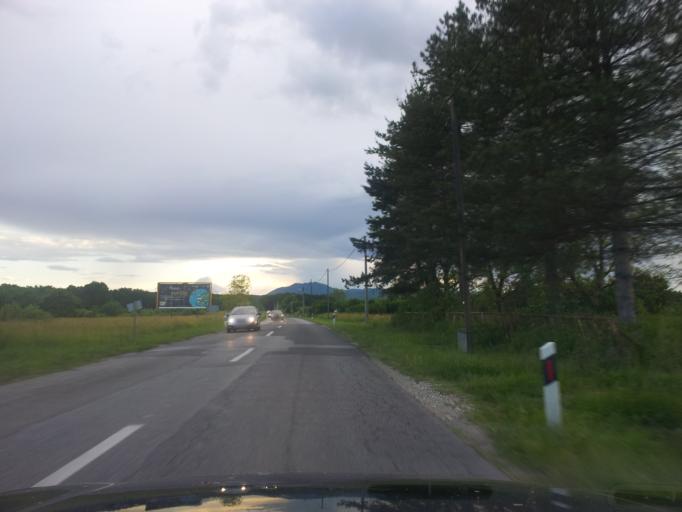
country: HR
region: Zagrebacka
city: Kerestinec
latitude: 45.7551
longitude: 15.8253
